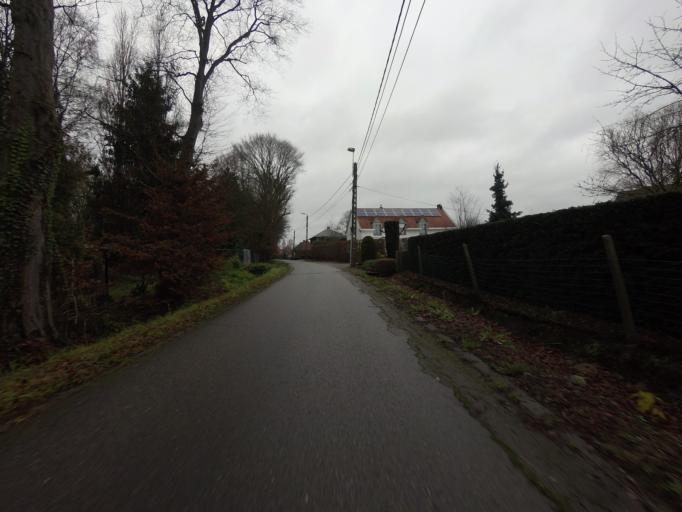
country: BE
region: Flanders
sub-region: Provincie Antwerpen
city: Sint-Katelijne-Waver
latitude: 51.0482
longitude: 4.5464
